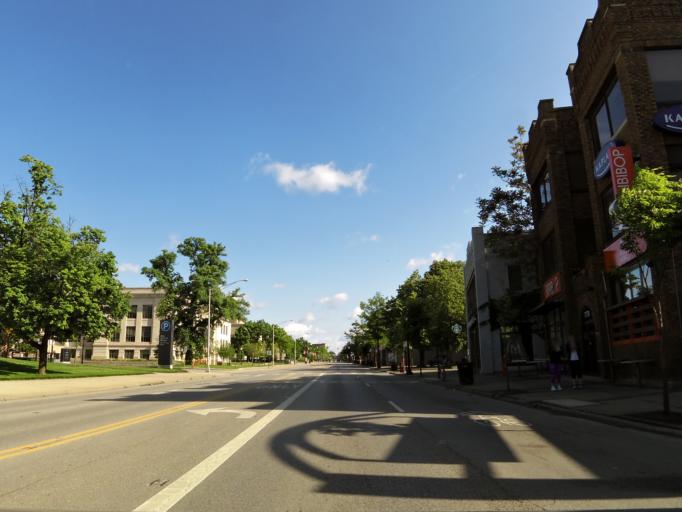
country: US
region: Ohio
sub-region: Franklin County
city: Grandview Heights
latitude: 39.9985
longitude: -83.0076
